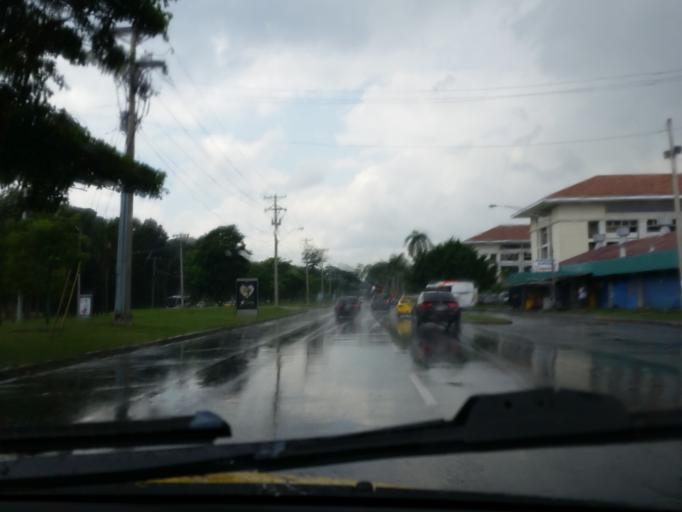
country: PA
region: Panama
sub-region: Distrito de Panama
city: Ancon
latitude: 8.9661
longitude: -79.5461
